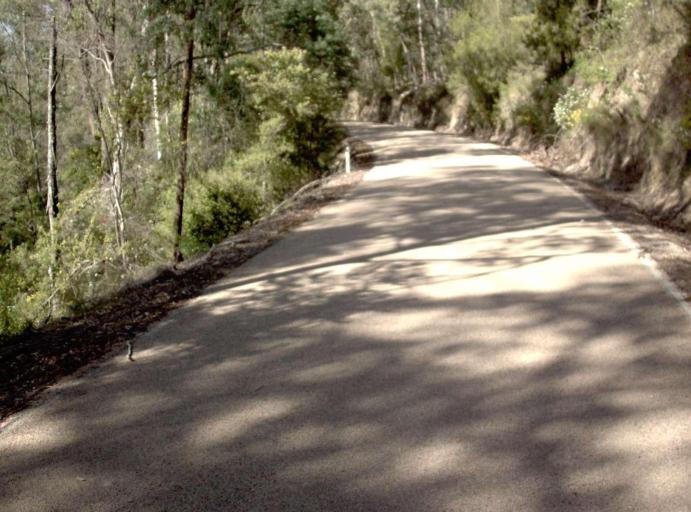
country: AU
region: Victoria
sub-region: East Gippsland
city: Lakes Entrance
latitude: -37.4964
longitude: 148.5532
